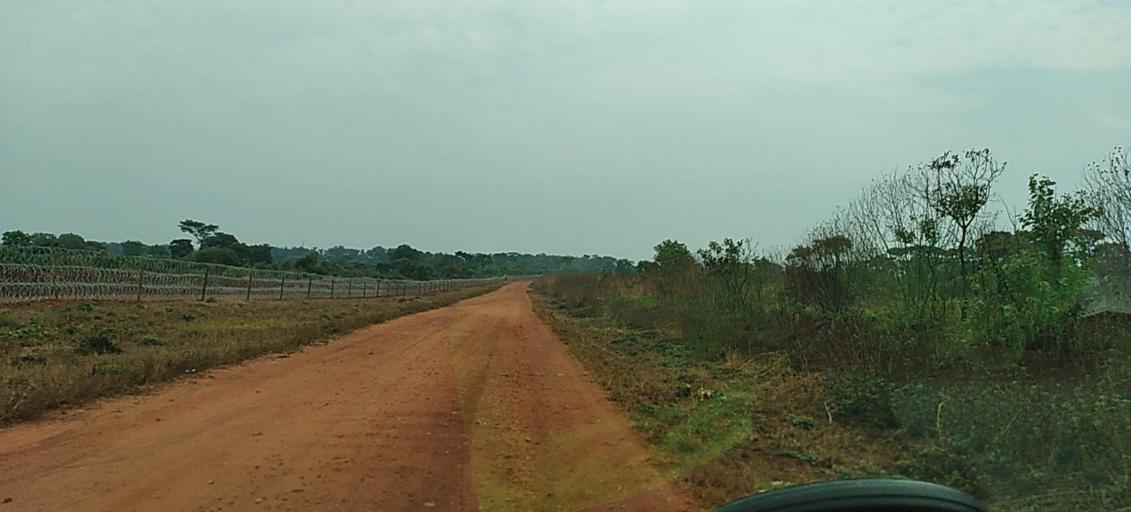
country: ZM
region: North-Western
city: Kansanshi
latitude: -12.1052
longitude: 26.4906
